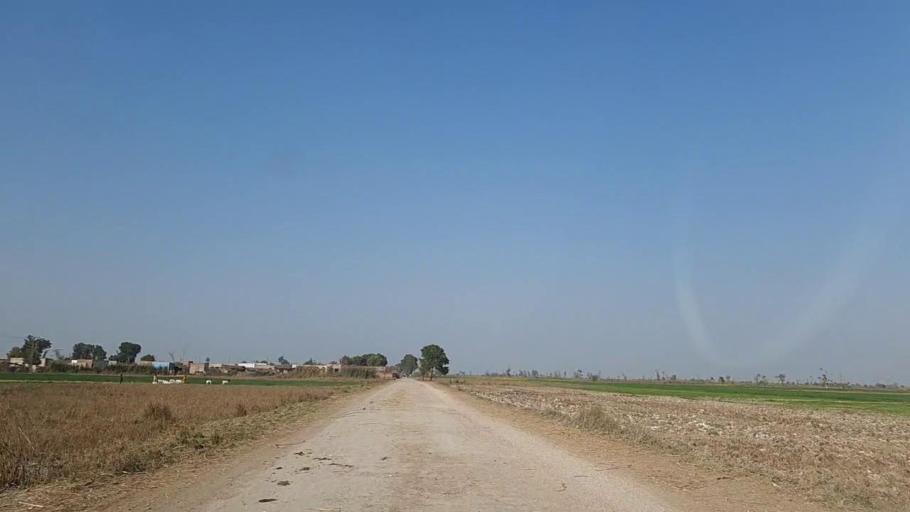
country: PK
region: Sindh
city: Daur
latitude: 26.4763
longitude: 68.2971
